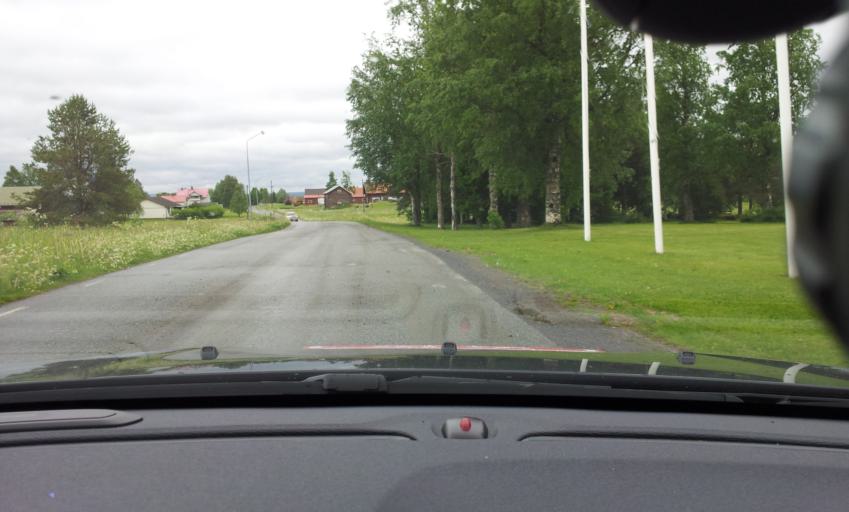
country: SE
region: Jaemtland
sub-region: Krokoms Kommun
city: Krokom
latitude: 63.6789
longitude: 14.6064
